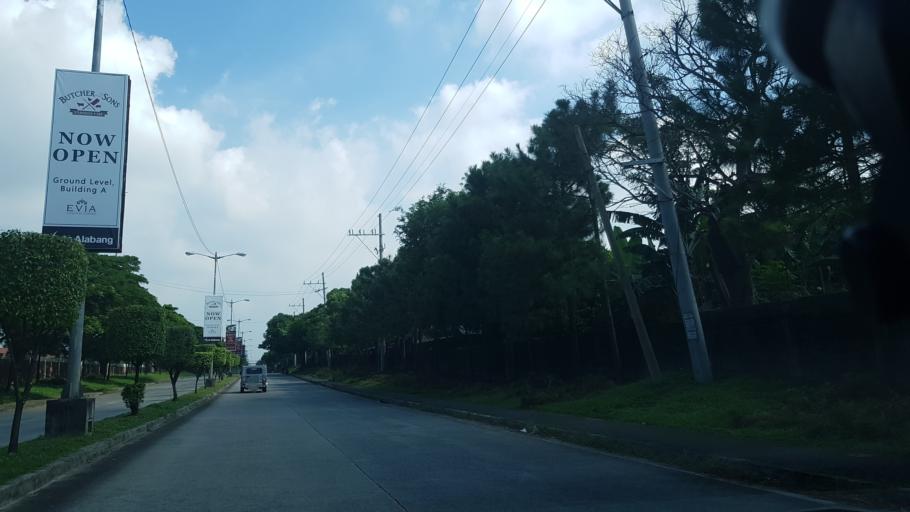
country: PH
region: Calabarzon
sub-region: Province of Laguna
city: Magsaysay
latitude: 14.3596
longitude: 121.0095
